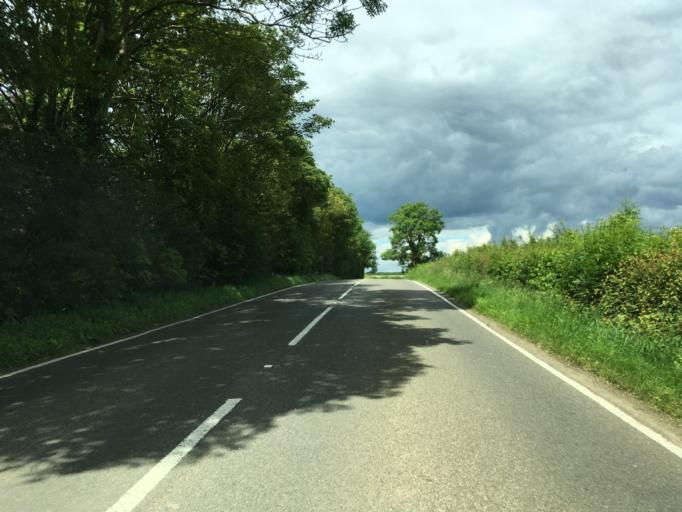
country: GB
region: England
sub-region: Northamptonshire
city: Brackley
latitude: 52.0876
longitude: -1.1925
